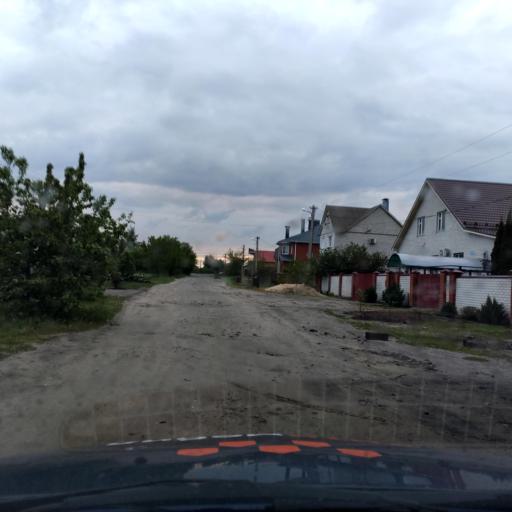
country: RU
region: Voronezj
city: Maslovka
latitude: 51.5462
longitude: 39.2396
